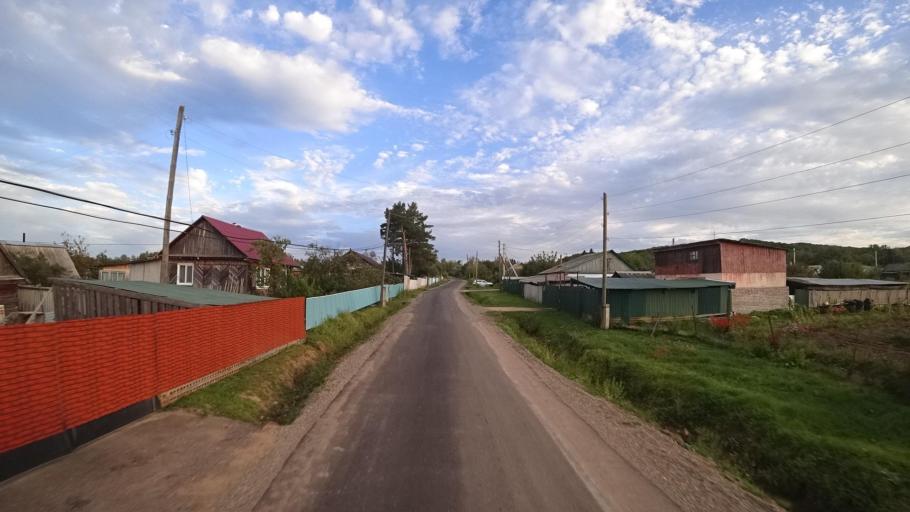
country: RU
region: Primorskiy
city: Yakovlevka
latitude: 44.4234
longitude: 133.4659
